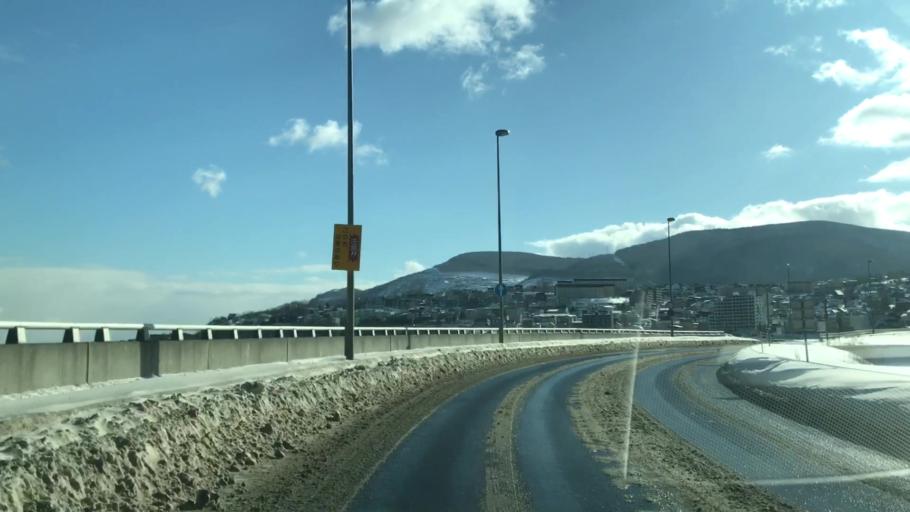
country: JP
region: Hokkaido
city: Otaru
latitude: 43.1824
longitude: 141.0361
